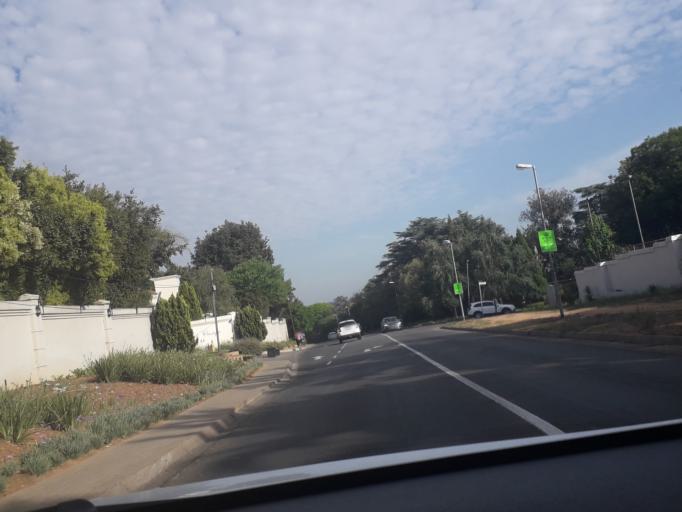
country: ZA
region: Gauteng
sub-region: City of Johannesburg Metropolitan Municipality
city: Johannesburg
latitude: -26.0721
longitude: 28.0055
